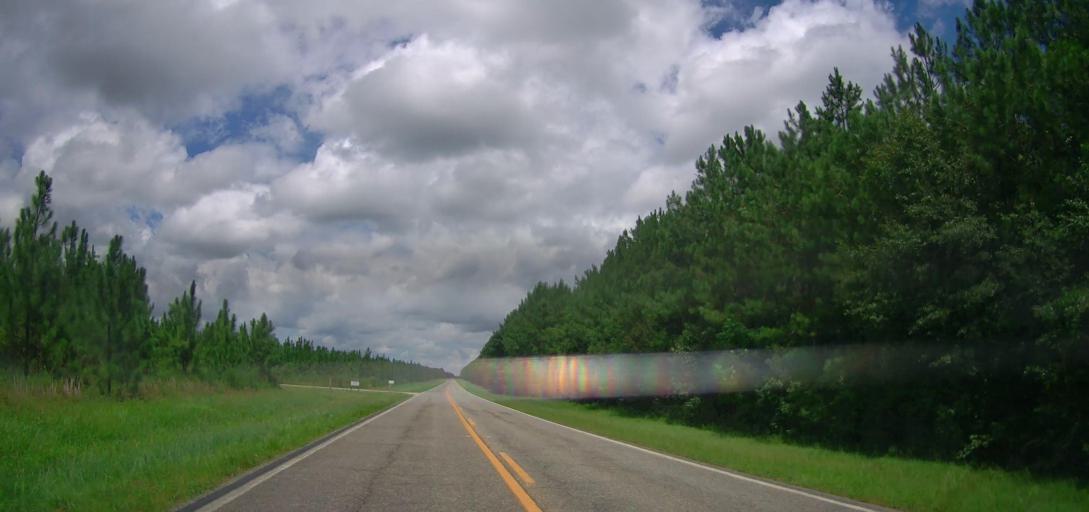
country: US
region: Georgia
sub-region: Wilcox County
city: Rochelle
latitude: 31.8619
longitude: -83.5584
